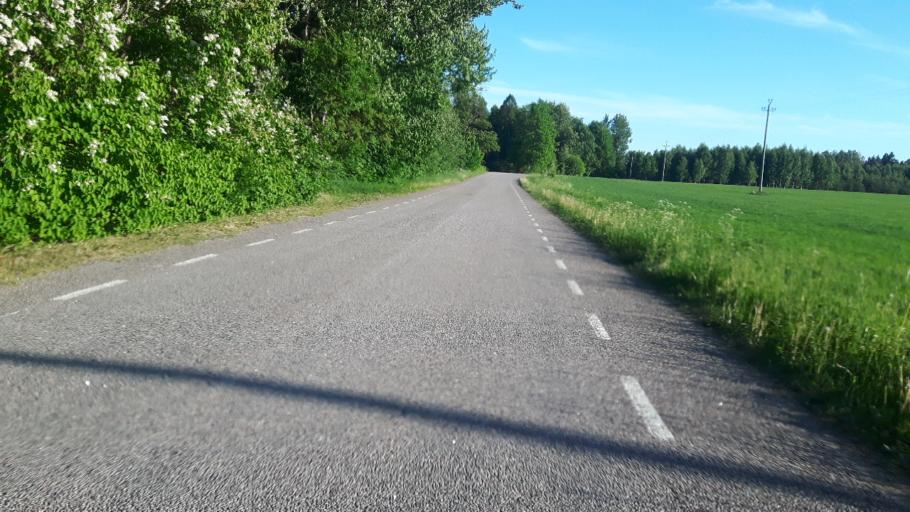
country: EE
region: Raplamaa
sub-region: Kehtna vald
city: Kehtna
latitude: 58.8932
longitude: 24.8794
